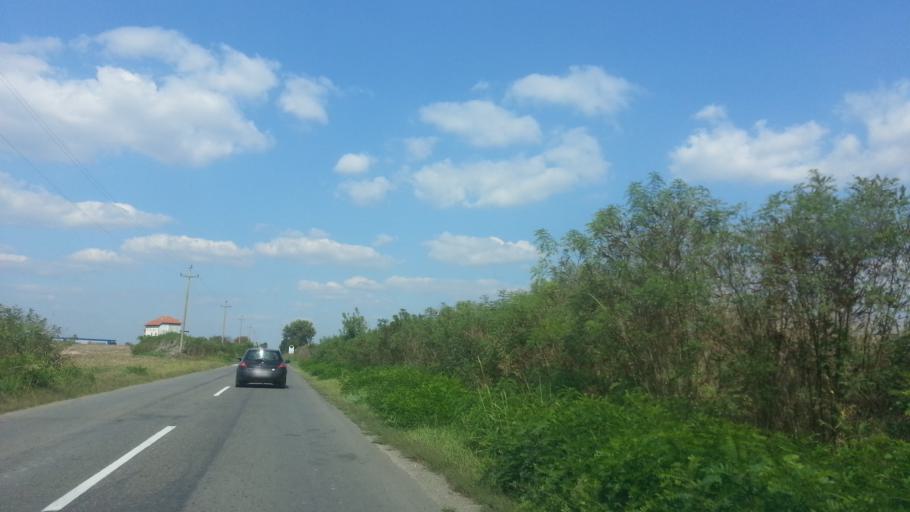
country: RS
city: Novi Banovci
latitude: 44.9304
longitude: 20.2798
